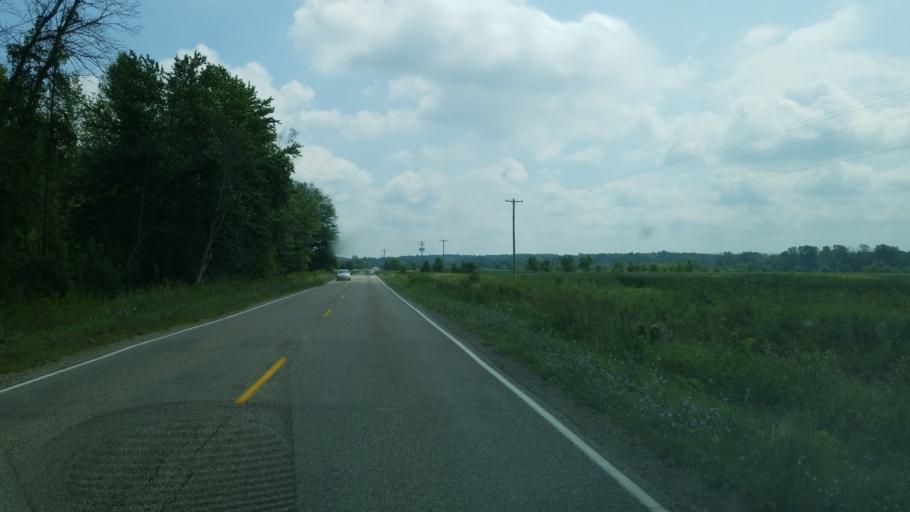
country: US
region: Michigan
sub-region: Kent County
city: Cedar Springs
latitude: 43.2202
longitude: -85.5242
